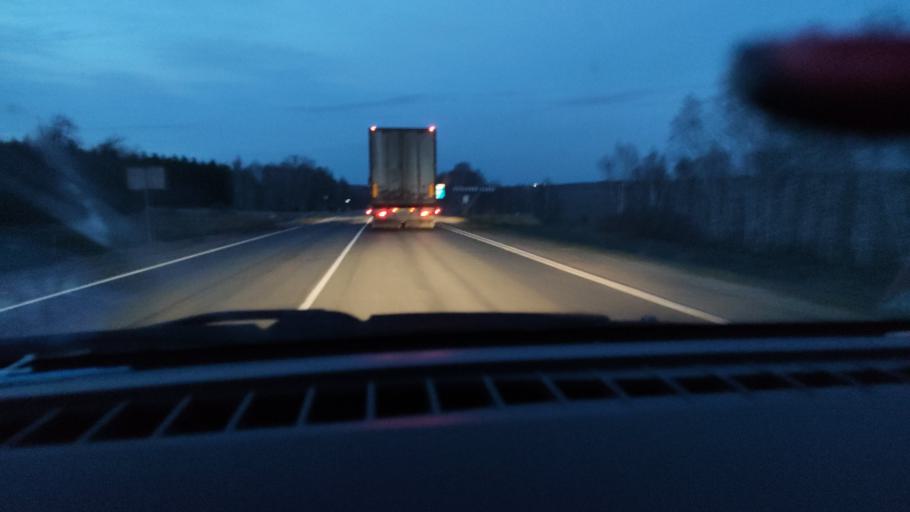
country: RU
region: Saratov
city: Sennoy
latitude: 52.1218
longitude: 46.8471
